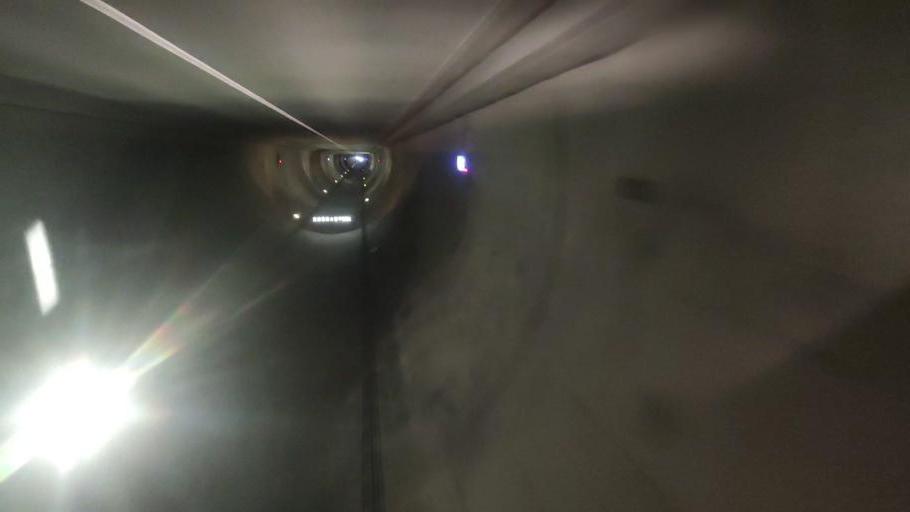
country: JP
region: Hokkaido
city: Iwamizawa
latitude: 43.0295
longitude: 142.0888
